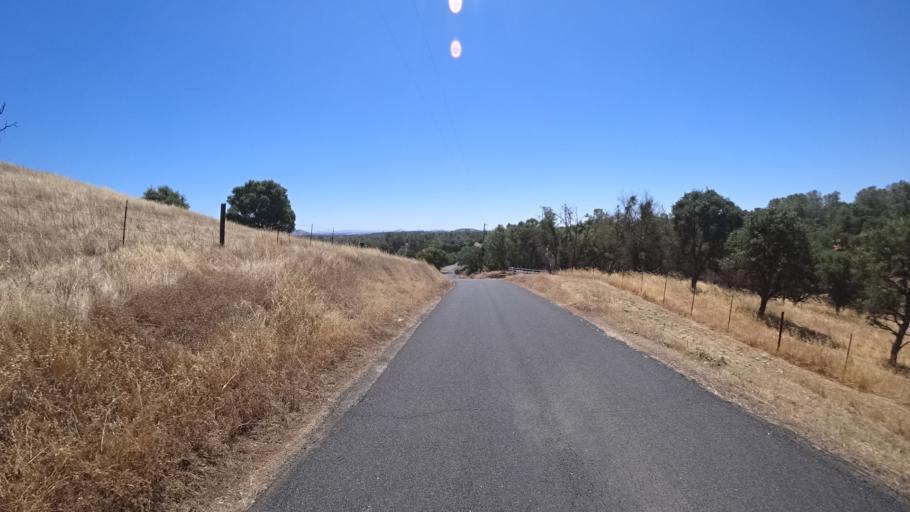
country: US
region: California
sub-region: Calaveras County
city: Copperopolis
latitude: 37.9648
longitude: -120.6873
